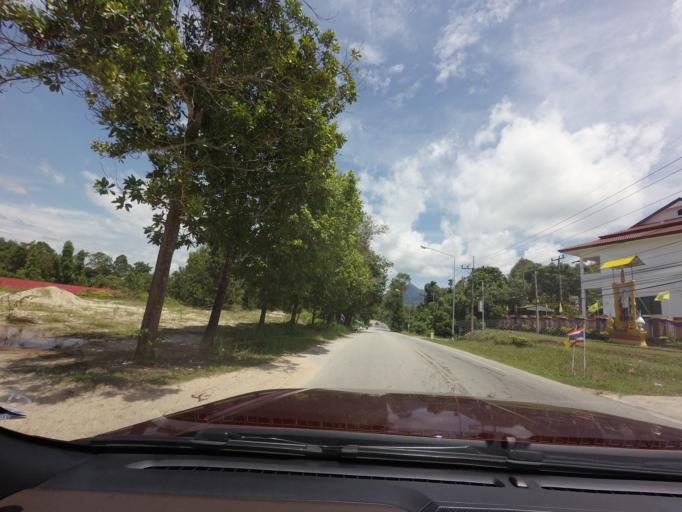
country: TH
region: Narathiwat
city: Ra-ngae
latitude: 6.2426
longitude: 101.6804
